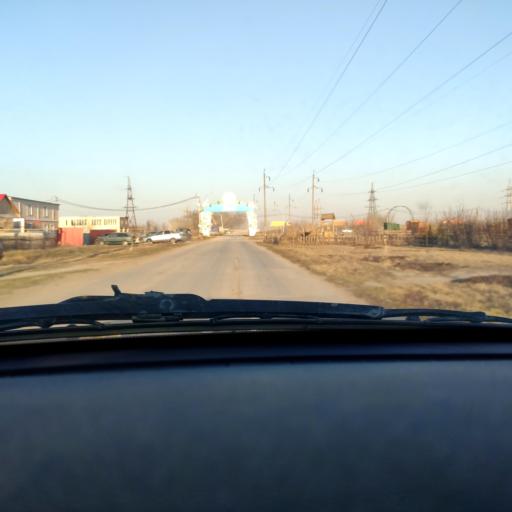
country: RU
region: Samara
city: Podstepki
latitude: 53.5691
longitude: 49.1206
